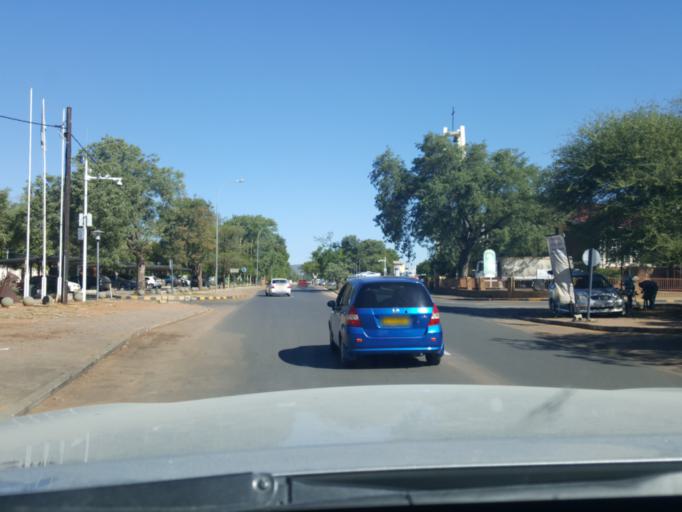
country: BW
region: South East
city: Gaborone
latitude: -24.6562
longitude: 25.9191
